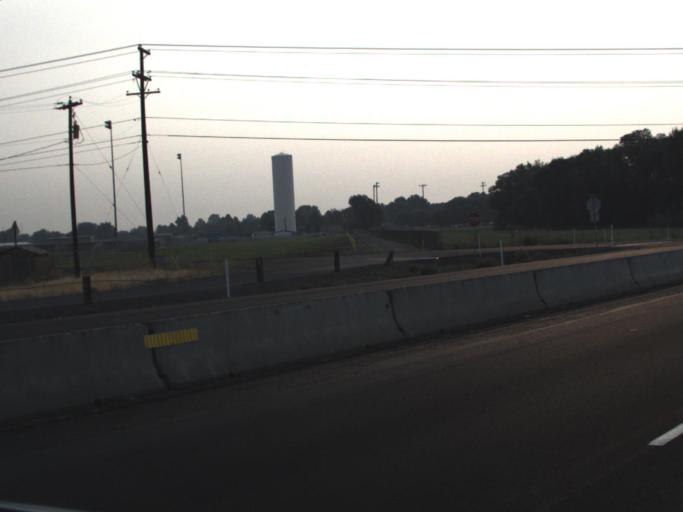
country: US
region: Washington
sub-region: Yakima County
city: Toppenish
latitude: 46.3785
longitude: -120.3366
